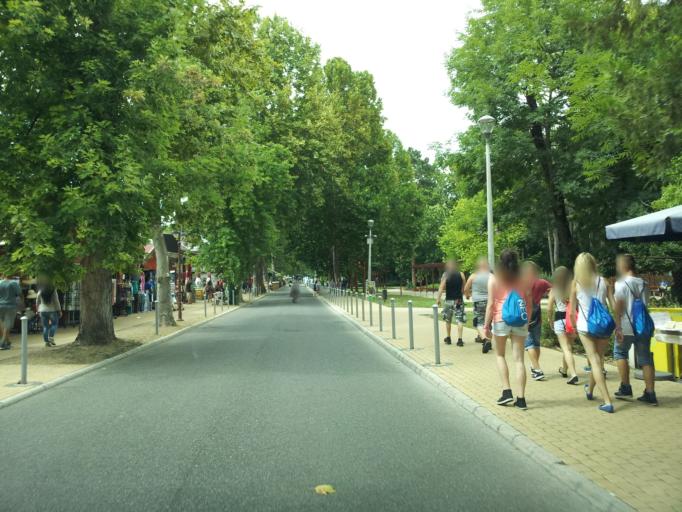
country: HU
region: Somogy
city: Siofok
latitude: 46.9077
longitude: 18.0478
